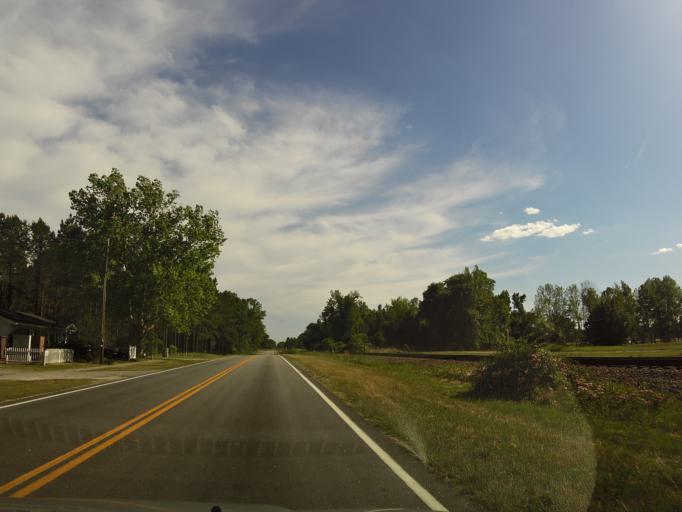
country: US
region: South Carolina
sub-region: Allendale County
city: Fairfax
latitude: 33.0356
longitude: -81.2222
